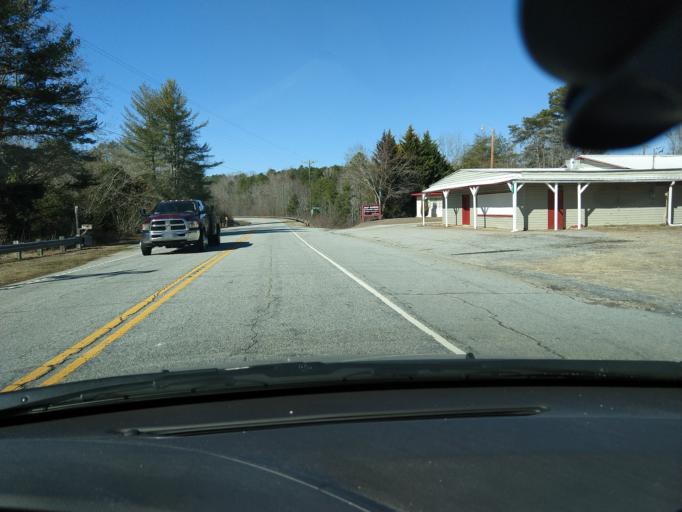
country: US
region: South Carolina
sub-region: Oconee County
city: Westminster
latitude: 34.6157
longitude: -83.1641
